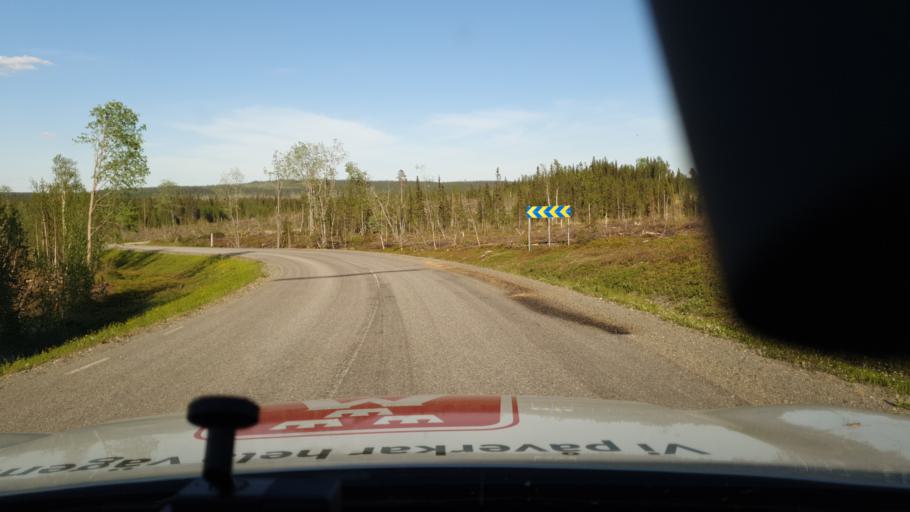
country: SE
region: Vaesterbotten
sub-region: Asele Kommun
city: Insjon
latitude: 64.7063
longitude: 17.2723
